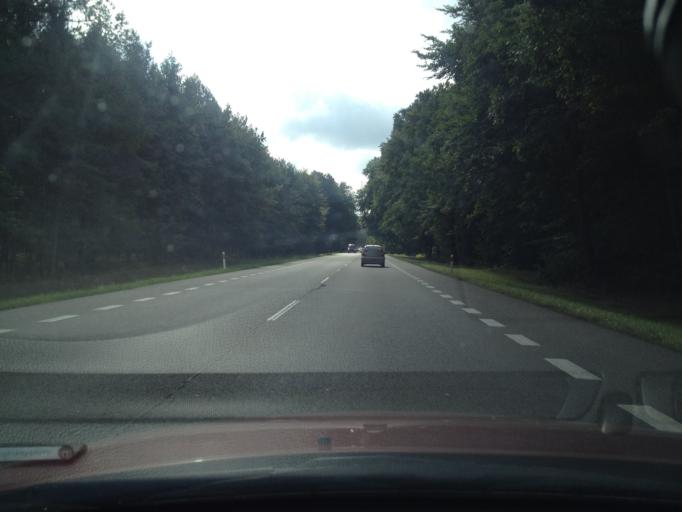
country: PL
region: West Pomeranian Voivodeship
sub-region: Powiat goleniowski
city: Przybiernow
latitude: 53.6918
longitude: 14.7940
